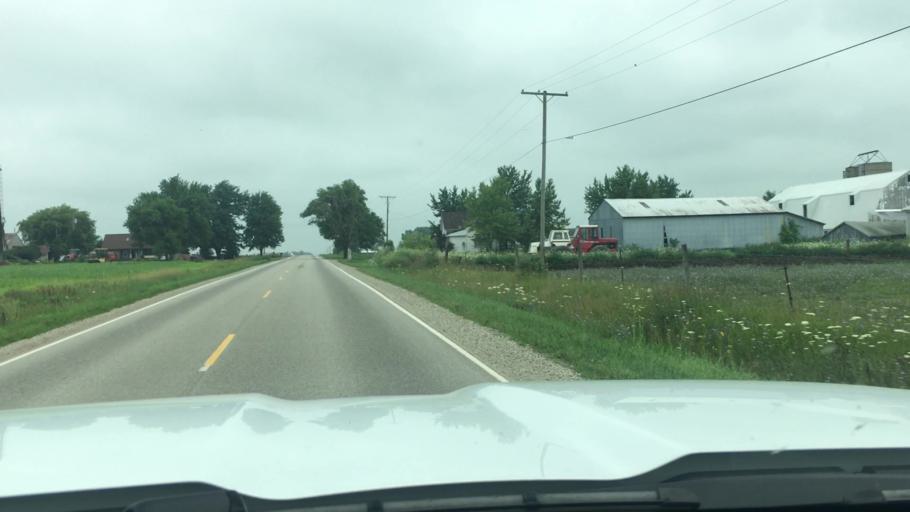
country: US
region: Michigan
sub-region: Sanilac County
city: Brown City
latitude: 43.2749
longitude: -82.9825
